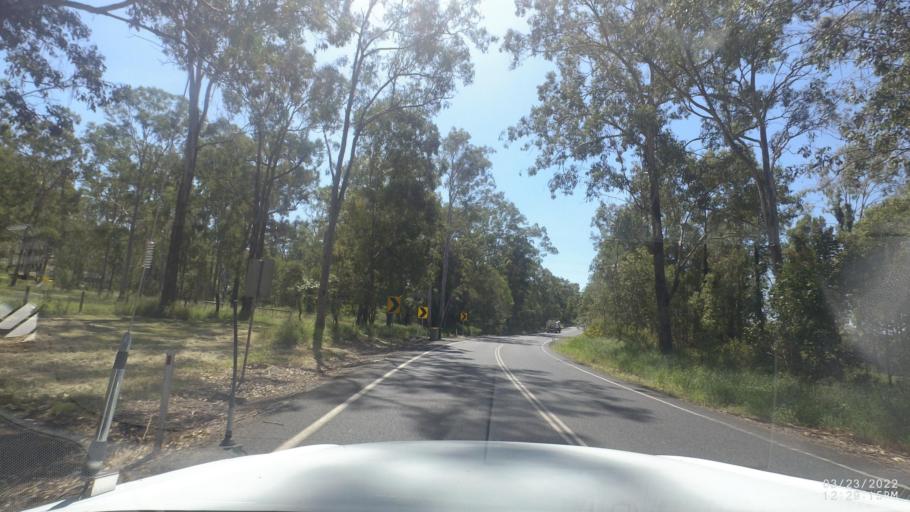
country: AU
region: Queensland
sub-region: Logan
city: Chambers Flat
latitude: -27.8067
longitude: 153.0974
